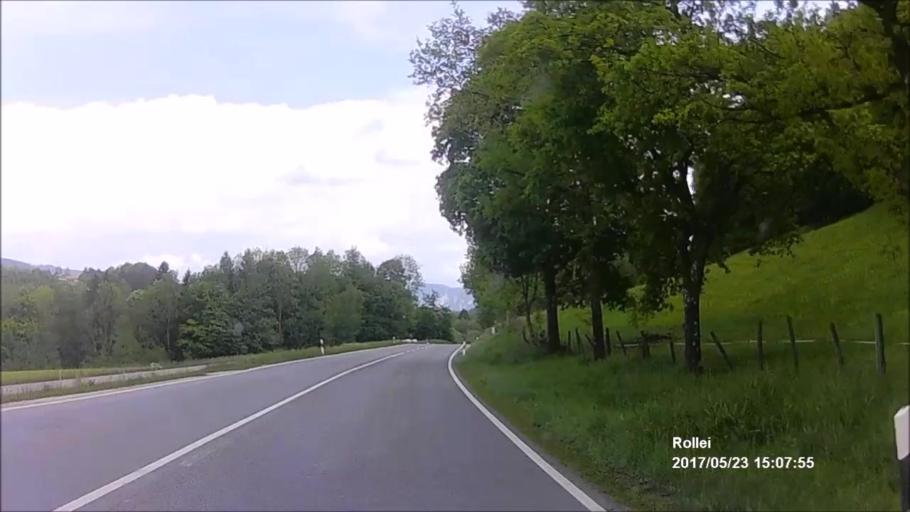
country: DE
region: Bavaria
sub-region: Upper Bavaria
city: Siegsdorf
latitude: 47.8156
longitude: 12.6799
